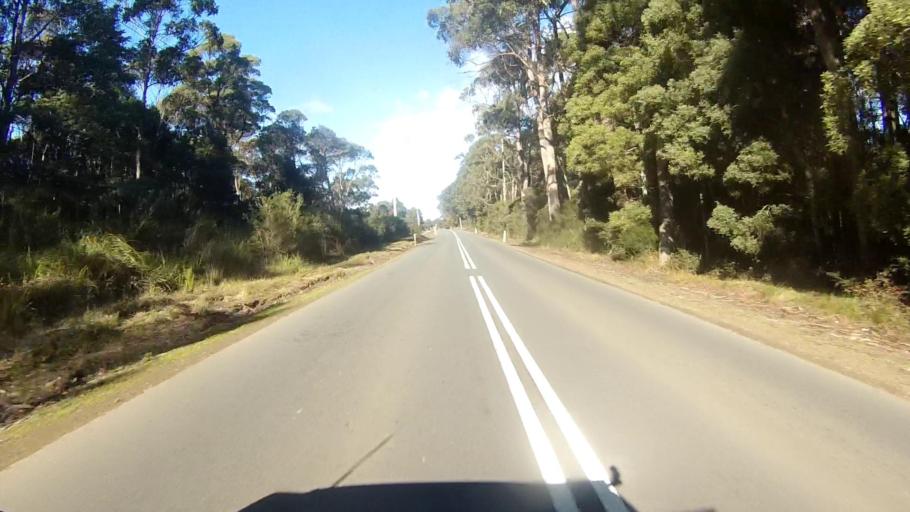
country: AU
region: Tasmania
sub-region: Clarence
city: Sandford
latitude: -43.0817
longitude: 147.8647
